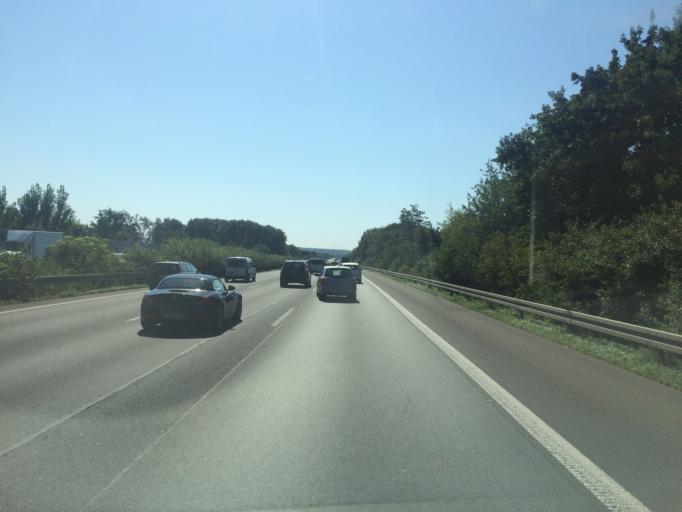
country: DE
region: North Rhine-Westphalia
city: Kamen
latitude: 51.5644
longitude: 7.6650
